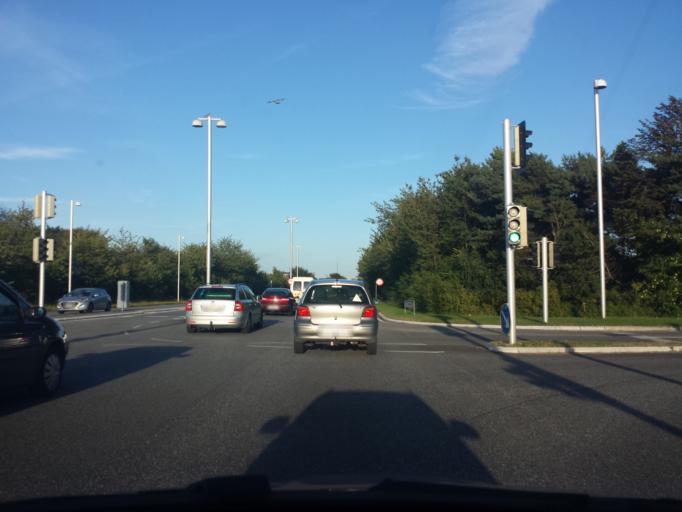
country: DK
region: Capital Region
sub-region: Egedal Kommune
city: Stenlose
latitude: 55.7792
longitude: 12.1749
